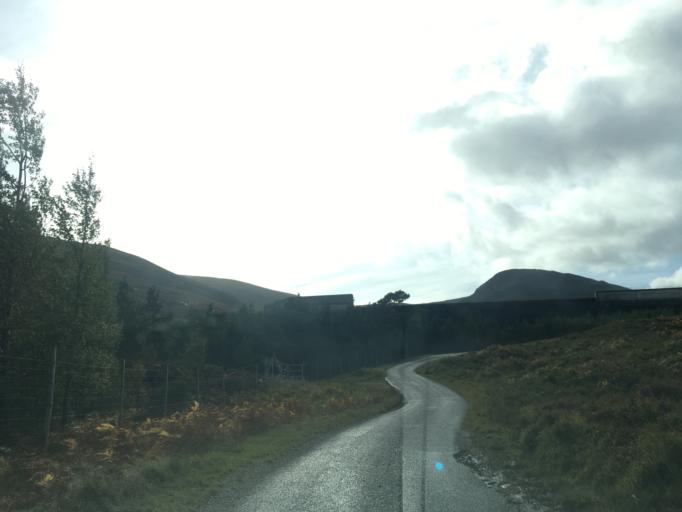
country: GB
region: Scotland
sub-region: Highland
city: Spean Bridge
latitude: 57.3405
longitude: -4.9541
